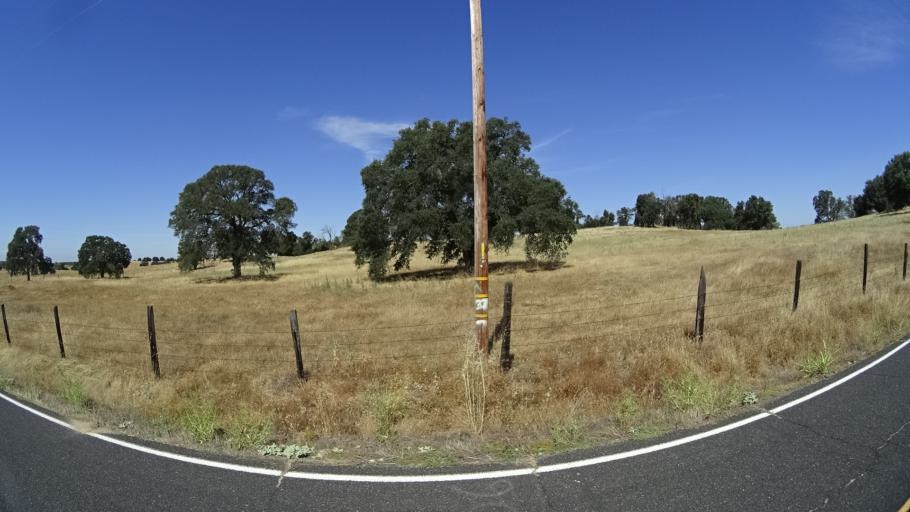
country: US
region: California
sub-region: Calaveras County
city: Rancho Calaveras
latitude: 38.1274
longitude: -120.9264
